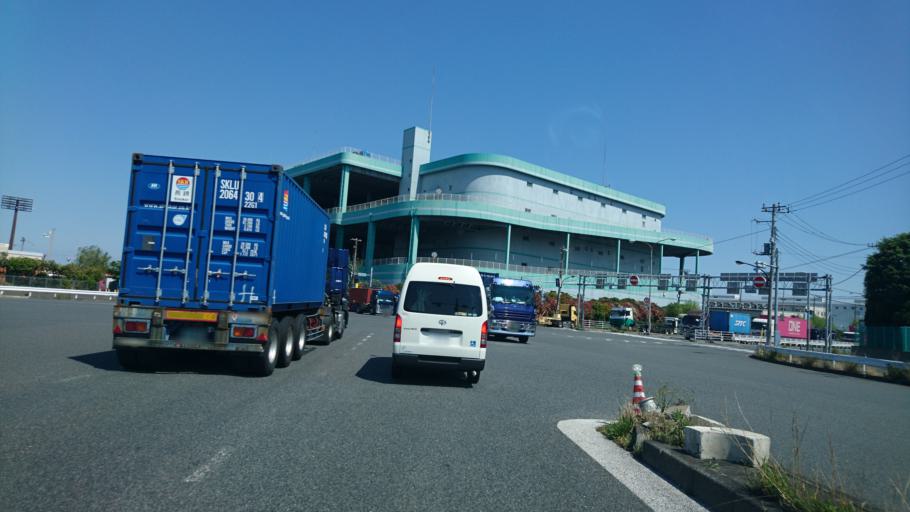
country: JP
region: Kanagawa
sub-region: Kawasaki-shi
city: Kawasaki
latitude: 35.5949
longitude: 139.7648
